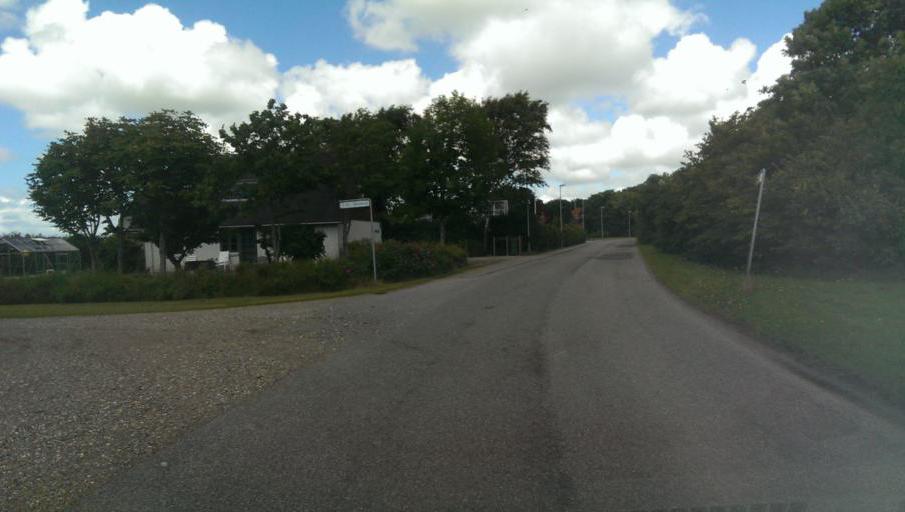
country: DK
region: Central Jutland
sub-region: Holstebro Kommune
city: Ulfborg
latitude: 56.2618
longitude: 8.2378
